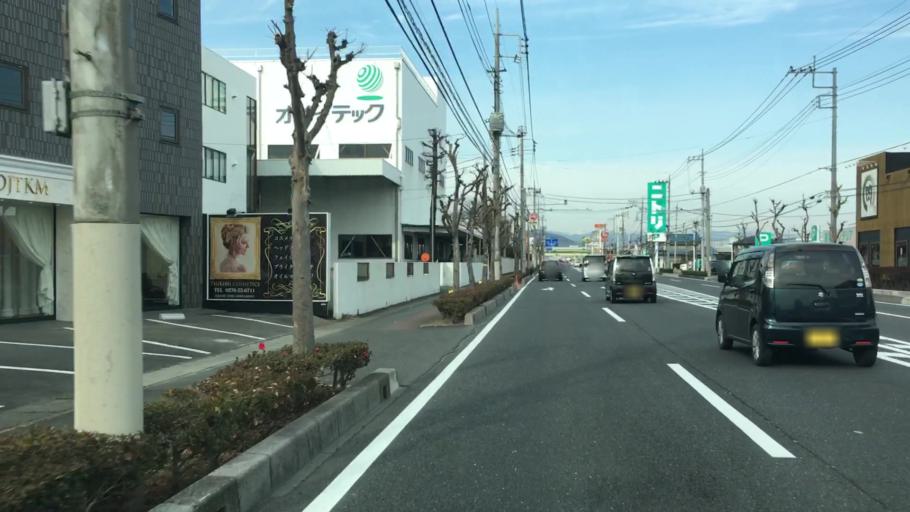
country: JP
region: Gunma
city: Ota
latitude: 36.2650
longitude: 139.3769
